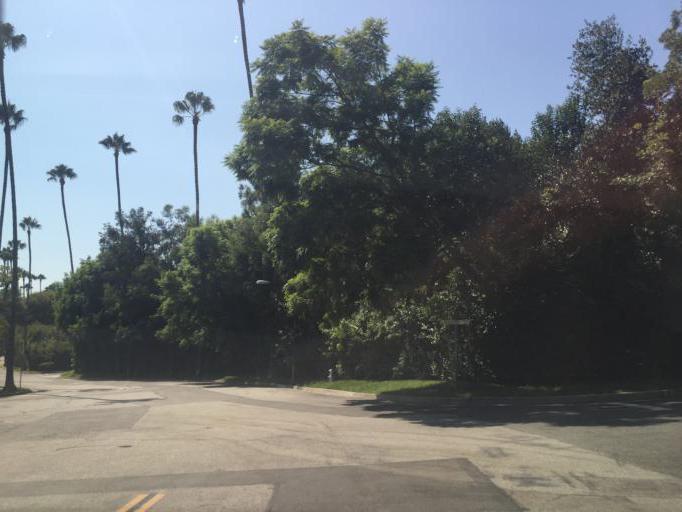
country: US
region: California
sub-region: Los Angeles County
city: Beverly Hills
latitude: 34.0900
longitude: -118.4036
